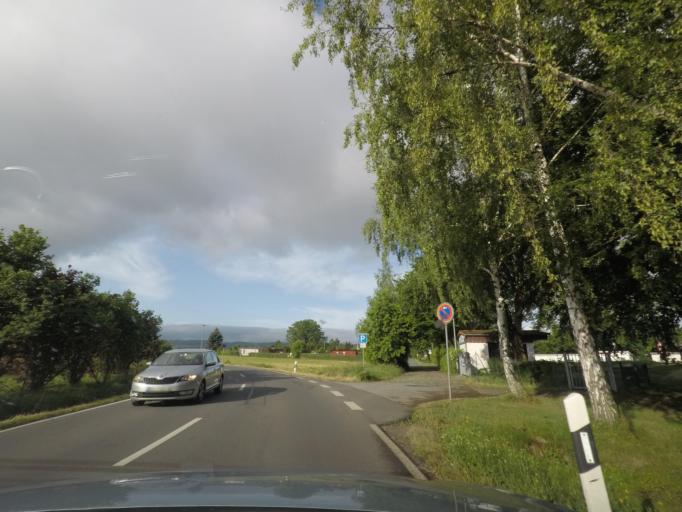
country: DE
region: Saxony-Anhalt
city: Derenburg
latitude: 51.8653
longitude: 10.9056
